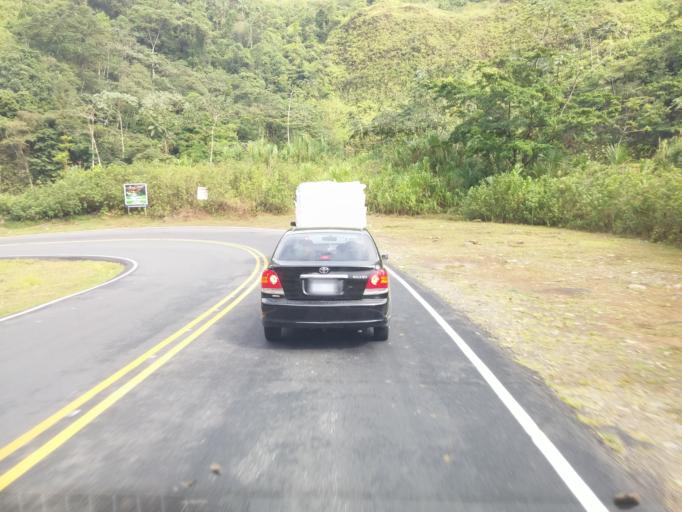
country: CR
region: Alajuela
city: San Ramon
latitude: 10.2166
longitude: -84.5442
